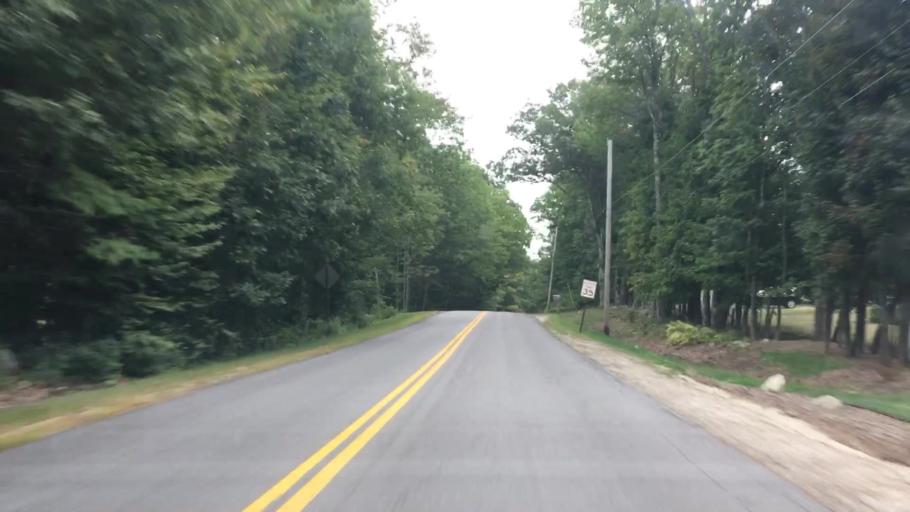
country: US
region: Maine
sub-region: Cumberland County
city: New Gloucester
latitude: 43.9099
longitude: -70.2254
